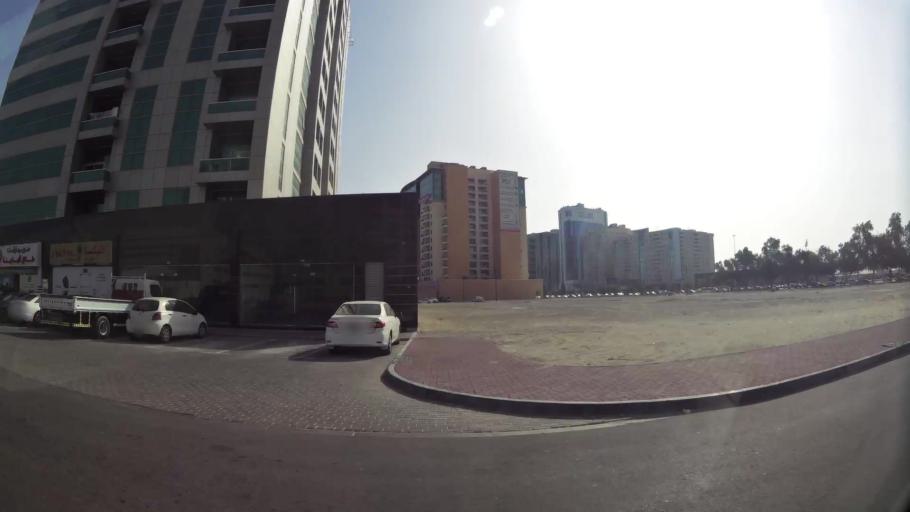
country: AE
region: Ash Shariqah
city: Sharjah
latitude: 25.2834
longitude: 55.3559
